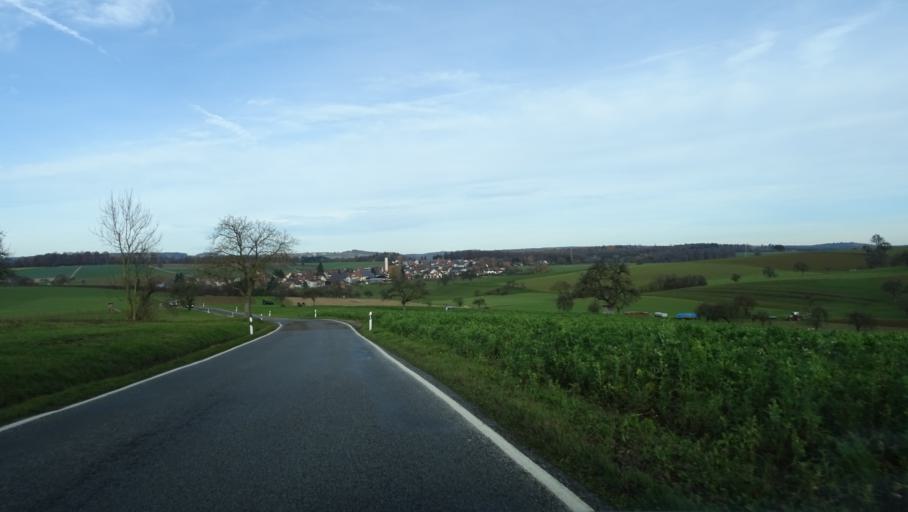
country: DE
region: Baden-Wuerttemberg
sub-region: Karlsruhe Region
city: Obrigheim
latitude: 49.3871
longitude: 9.1010
